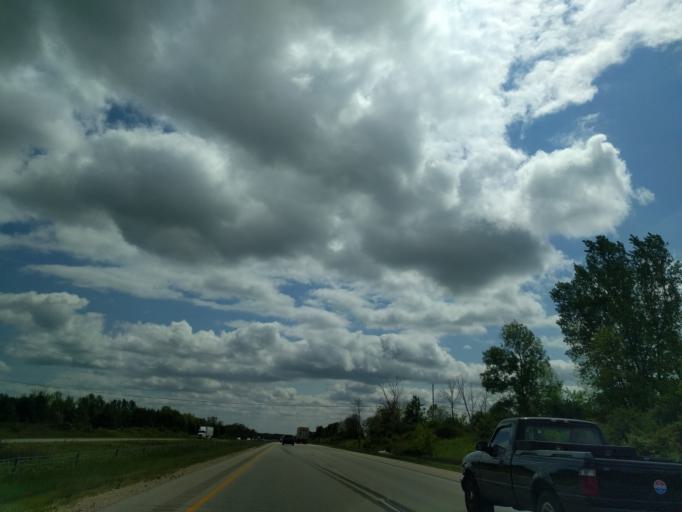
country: US
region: Wisconsin
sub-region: Ozaukee County
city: Thiensville
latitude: 43.2441
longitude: -87.9200
